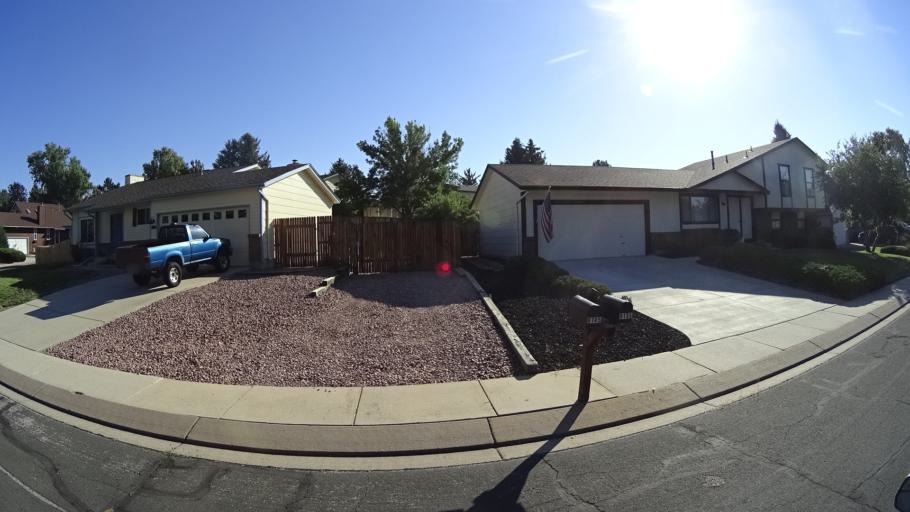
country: US
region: Colorado
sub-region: El Paso County
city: Black Forest
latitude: 38.9507
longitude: -104.7675
